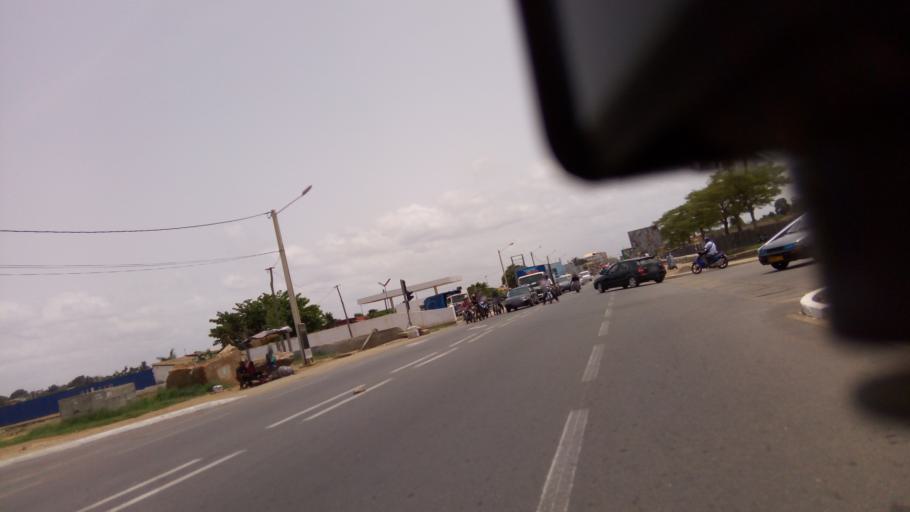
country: TG
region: Maritime
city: Lome
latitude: 6.1403
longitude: 1.2211
